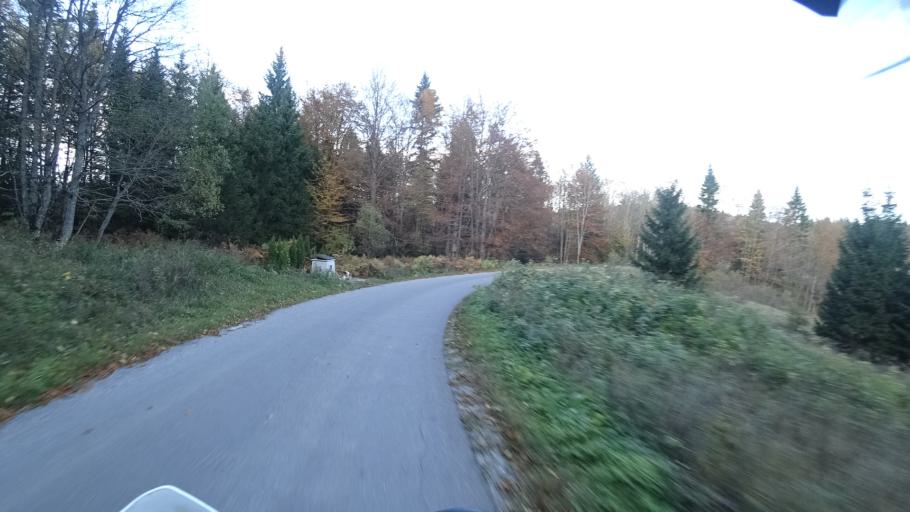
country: HR
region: Karlovacka
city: Plaski
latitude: 44.9735
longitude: 15.3962
